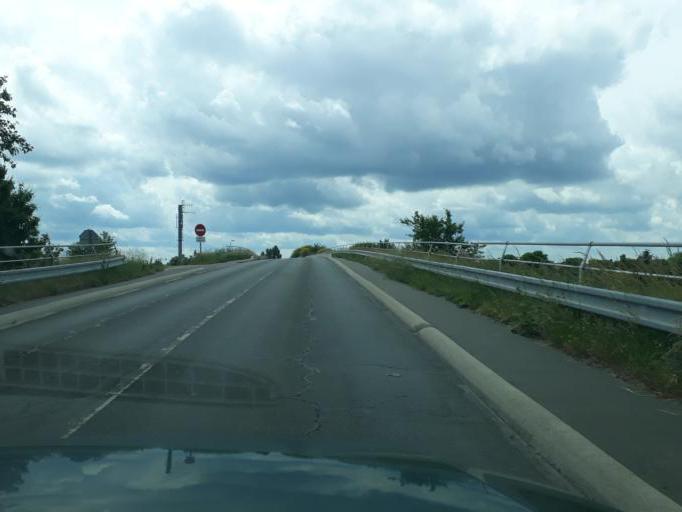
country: FR
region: Centre
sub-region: Departement du Loiret
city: La Chapelle-Saint-Mesmin
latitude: 47.9009
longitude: 1.8361
